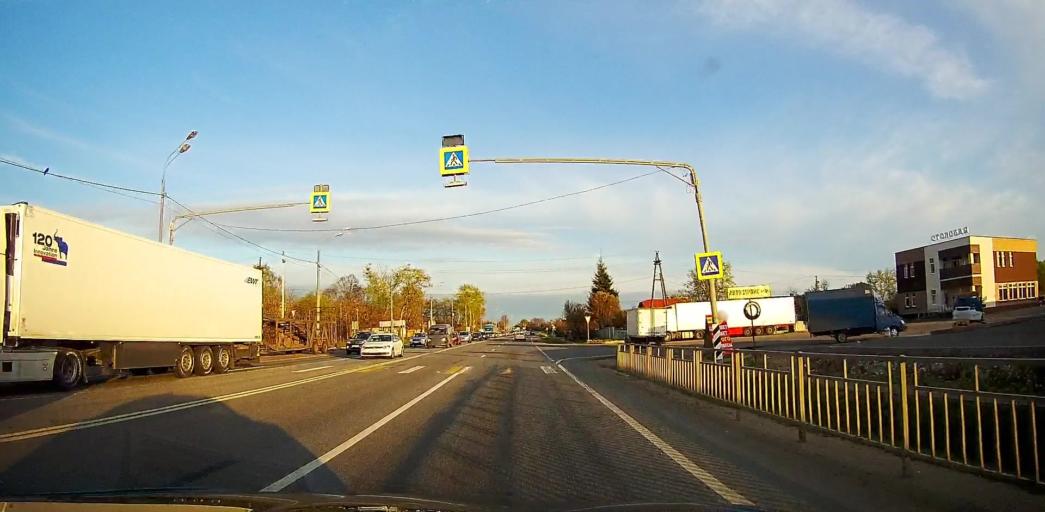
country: RU
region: Moskovskaya
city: Troitskoye
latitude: 55.2482
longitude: 38.5277
